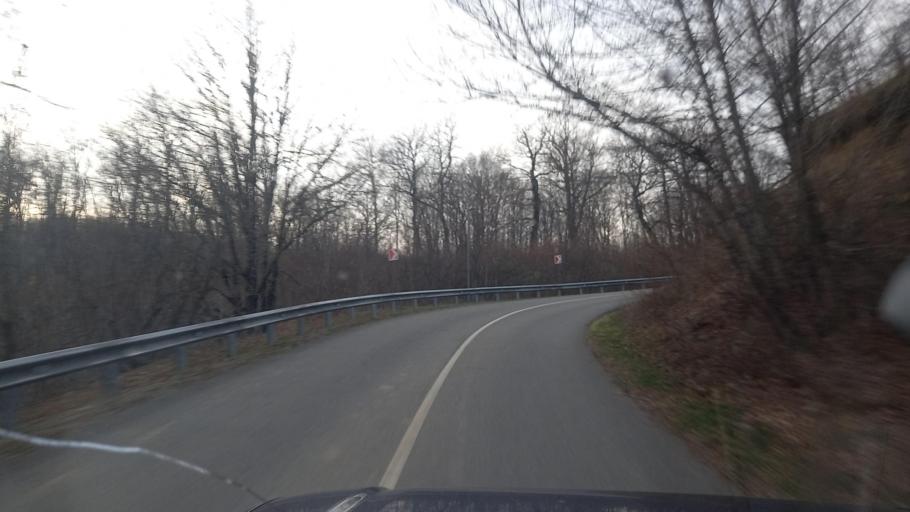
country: RU
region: Krasnodarskiy
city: Goryachiy Klyuch
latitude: 44.3866
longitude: 39.1834
